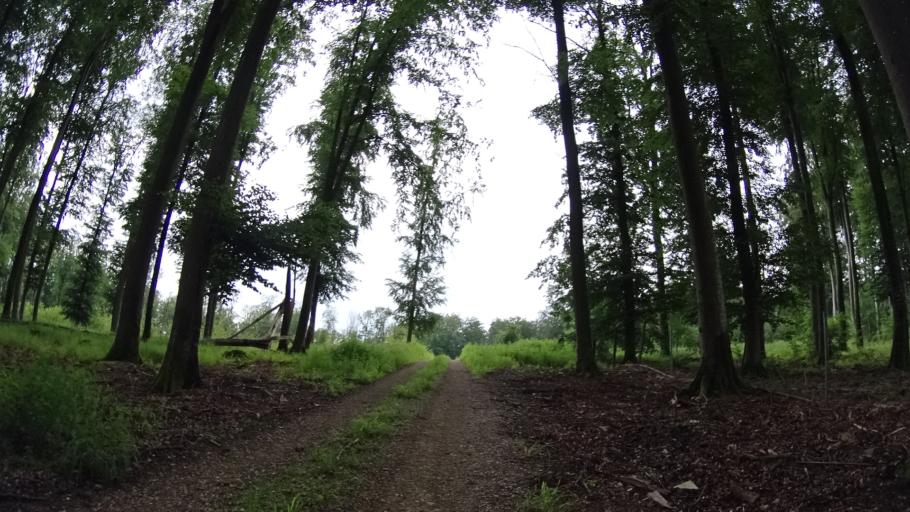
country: DE
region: Bavaria
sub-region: Upper Bavaria
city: Denkendorf
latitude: 48.9023
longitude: 11.4770
